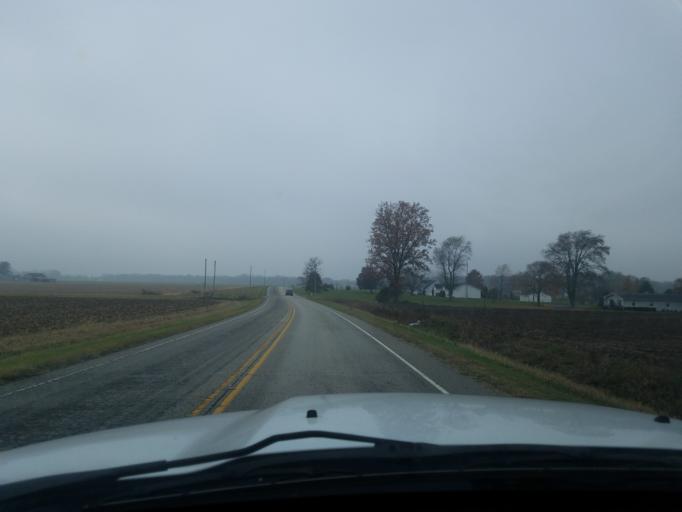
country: US
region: Indiana
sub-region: Cass County
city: Walton
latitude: 40.7577
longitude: -86.2060
